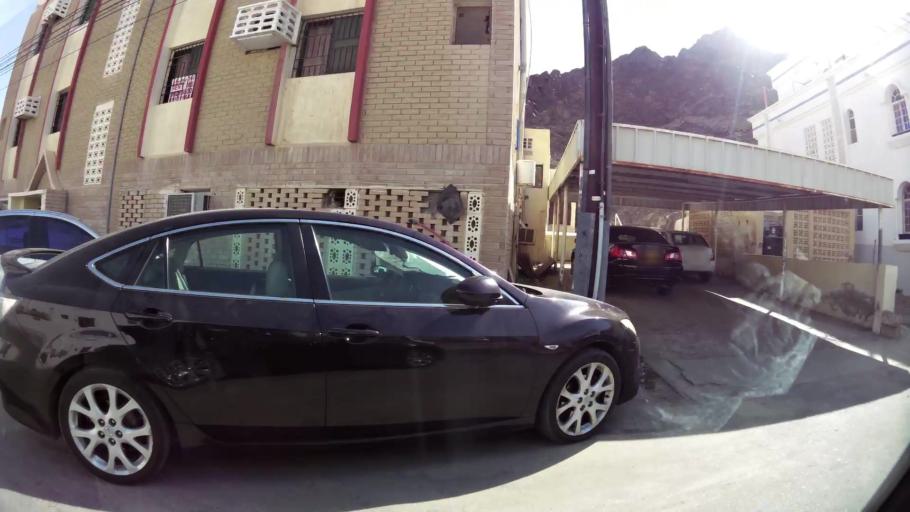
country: OM
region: Muhafazat Masqat
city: Muscat
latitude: 23.6048
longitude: 58.5538
